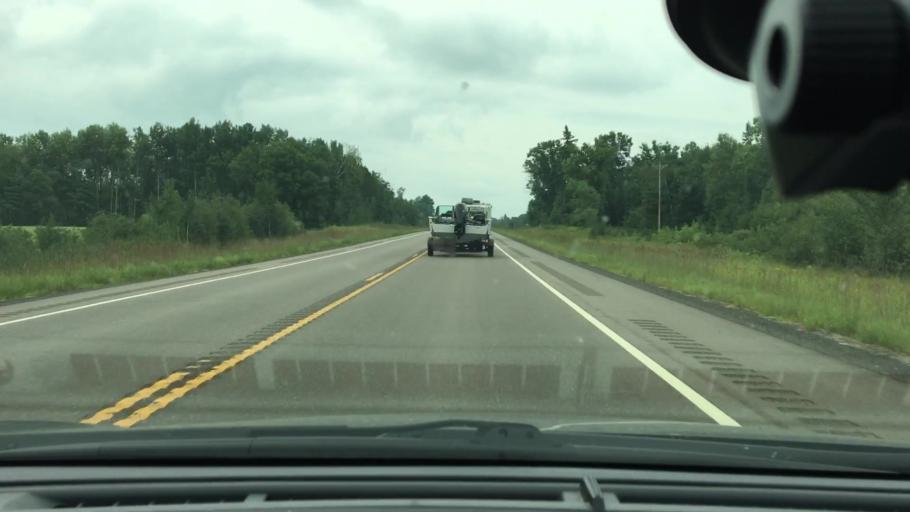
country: US
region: Minnesota
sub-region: Crow Wing County
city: Crosby
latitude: 46.5770
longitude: -93.9527
